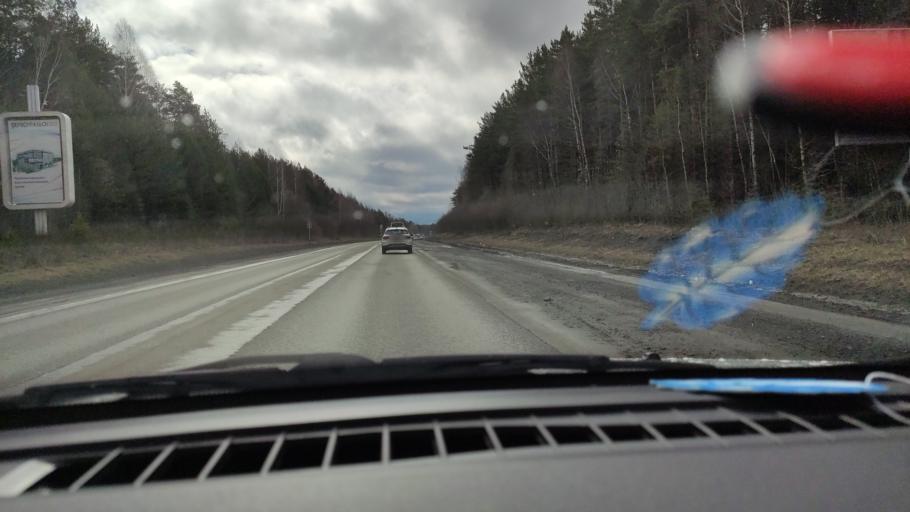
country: RU
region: Sverdlovsk
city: Talitsa
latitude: 56.8693
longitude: 60.0420
